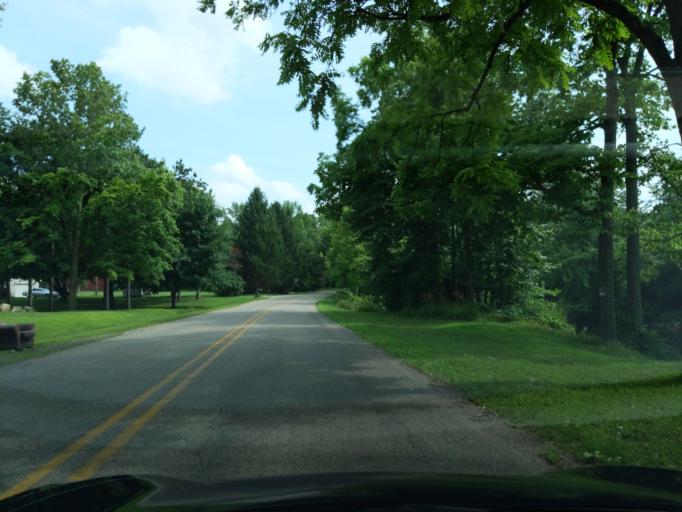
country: US
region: Michigan
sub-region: Eaton County
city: Dimondale
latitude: 42.5802
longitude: -84.6013
